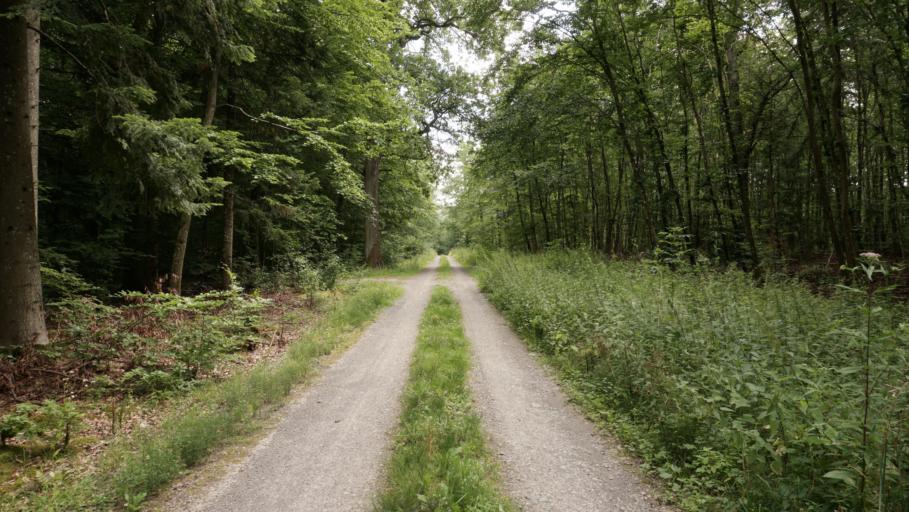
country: DE
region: Baden-Wuerttemberg
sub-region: Karlsruhe Region
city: Hassmersheim
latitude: 49.3245
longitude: 9.1933
